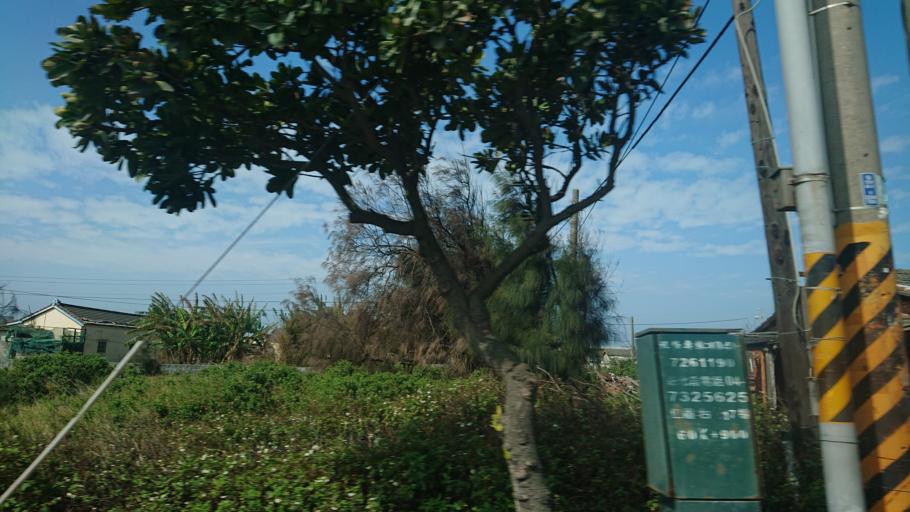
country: TW
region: Taiwan
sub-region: Yunlin
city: Douliu
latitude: 23.9016
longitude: 120.3066
